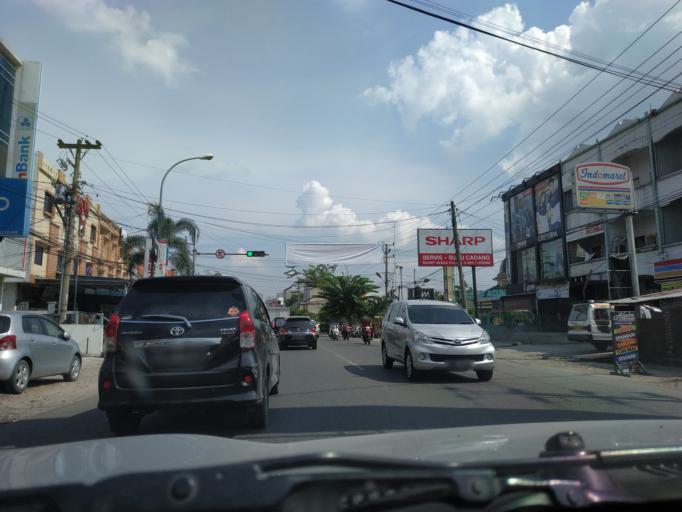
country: ID
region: North Sumatra
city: Rantauprapat
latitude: 2.0957
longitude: 99.8337
